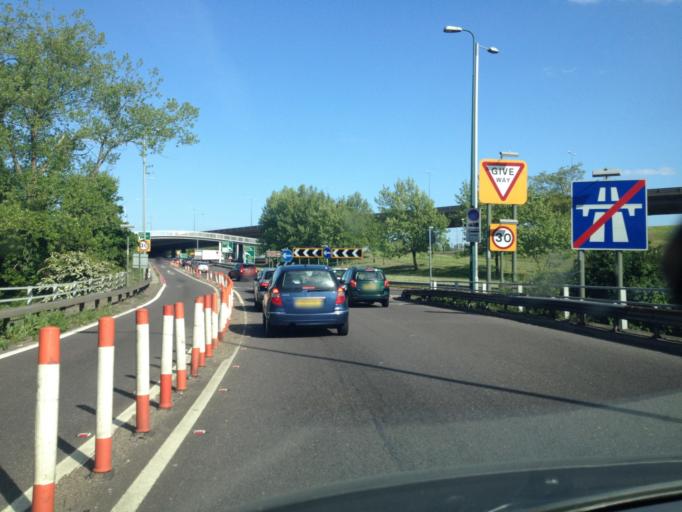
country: GB
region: England
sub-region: Greater London
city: Hendon
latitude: 51.5733
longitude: -0.2304
